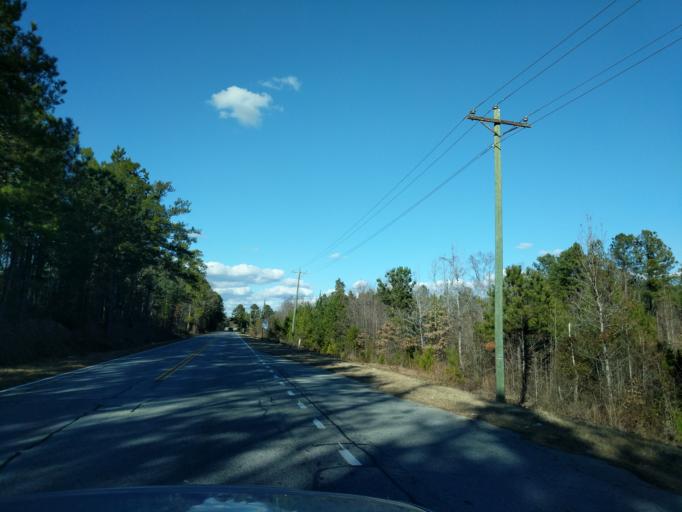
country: US
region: South Carolina
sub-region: Greenwood County
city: Ninety Six
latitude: 34.2909
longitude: -82.0465
